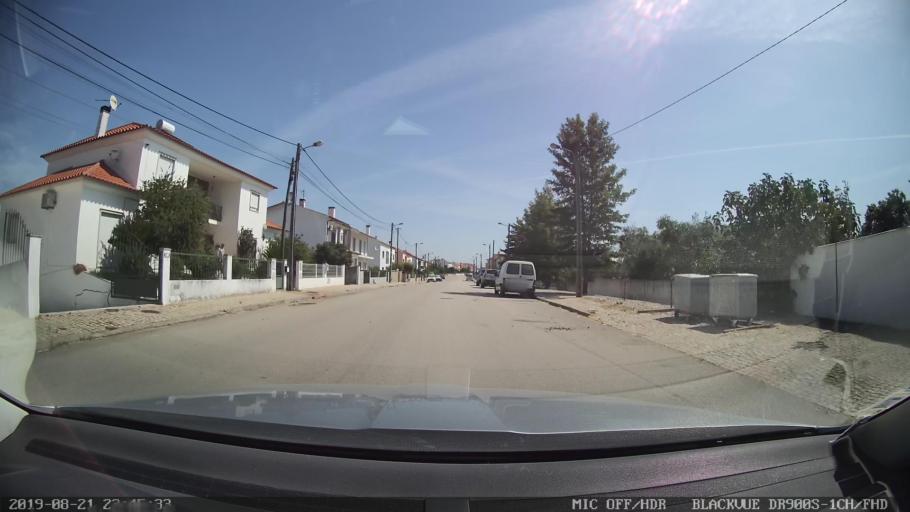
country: PT
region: Castelo Branco
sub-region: Idanha-A-Nova
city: Idanha-a-Nova
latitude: 39.8383
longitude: -7.2637
